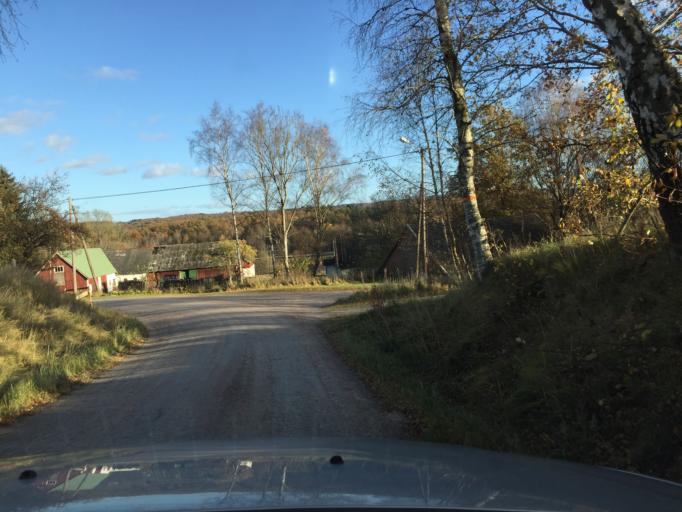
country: SE
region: Skane
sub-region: Hassleholms Kommun
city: Tormestorp
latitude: 56.0657
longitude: 13.7247
